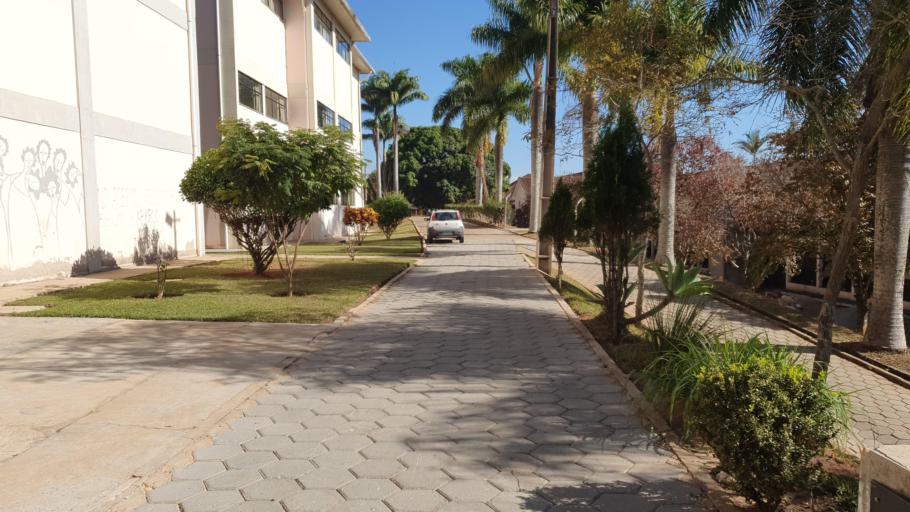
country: BR
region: Minas Gerais
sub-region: Sao Joao Del Rei
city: Sao Joao del Rei
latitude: -21.1046
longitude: -44.2484
